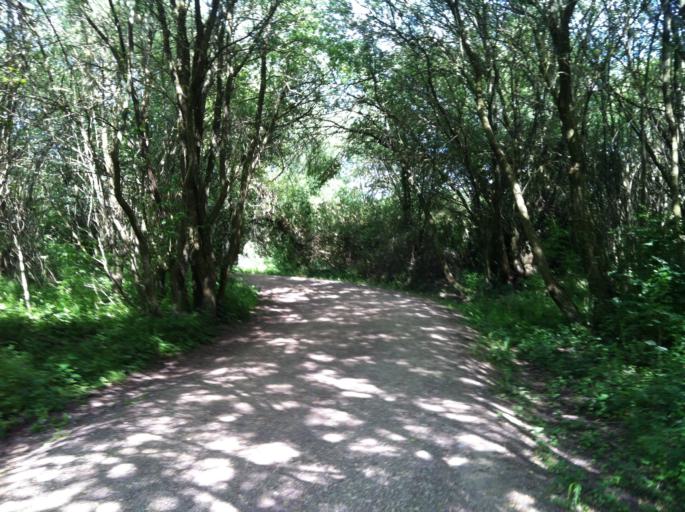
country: ES
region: Basque Country
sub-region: Provincia de Alava
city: Gasteiz / Vitoria
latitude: 42.8555
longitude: -2.6433
